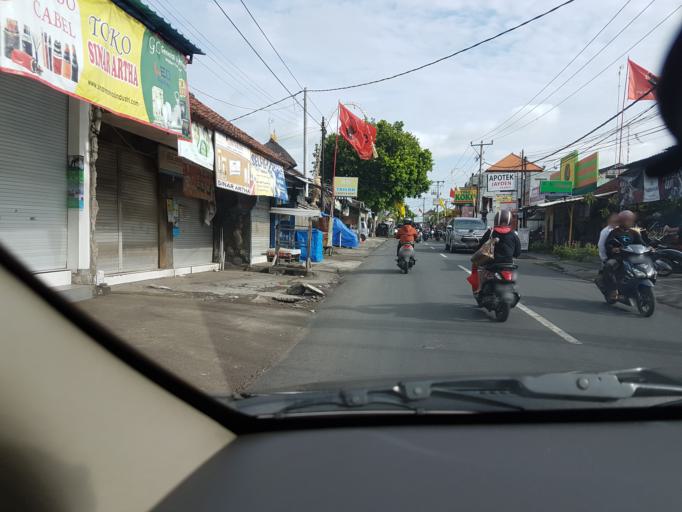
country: ID
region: Bali
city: Kuta
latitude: -8.6797
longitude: 115.1806
